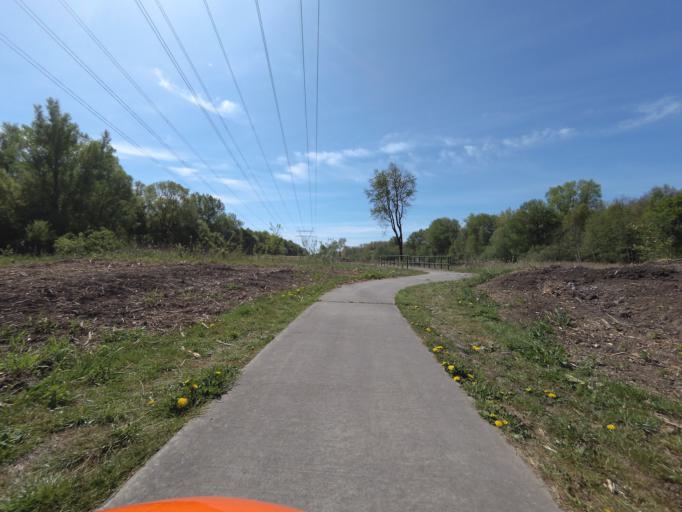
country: NL
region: Gelderland
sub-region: Gemeente Harderwijk
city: Harderwijk
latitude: 52.4044
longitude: 5.6231
